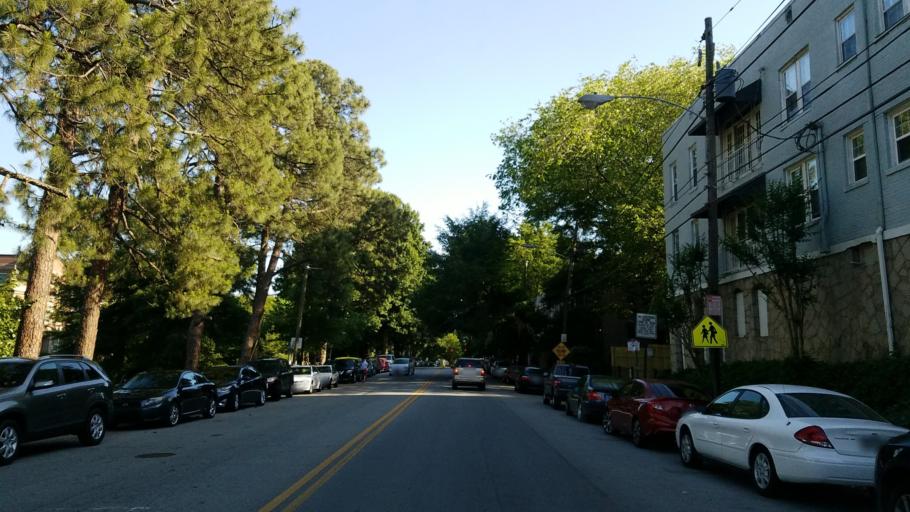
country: US
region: Georgia
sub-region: Fulton County
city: Atlanta
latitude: 33.7815
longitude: -84.3728
